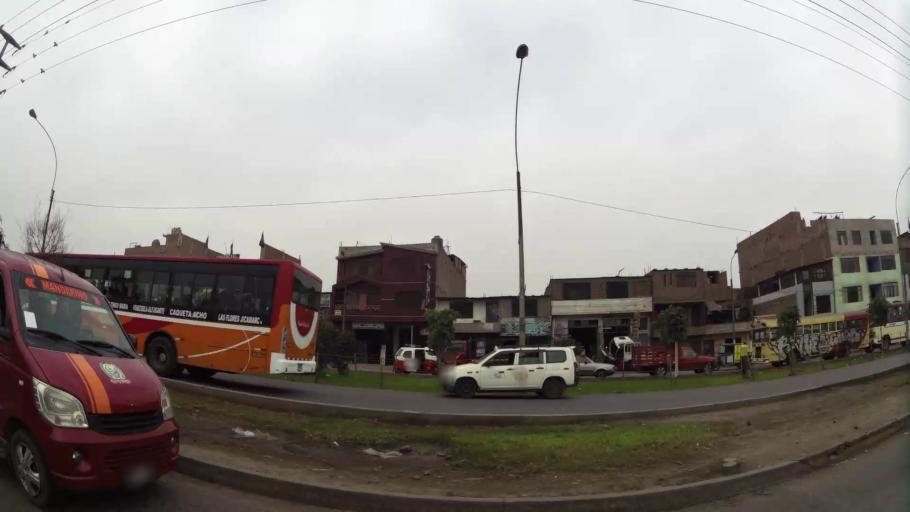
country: PE
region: Lima
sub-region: Lima
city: Independencia
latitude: -11.9668
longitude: -77.0019
